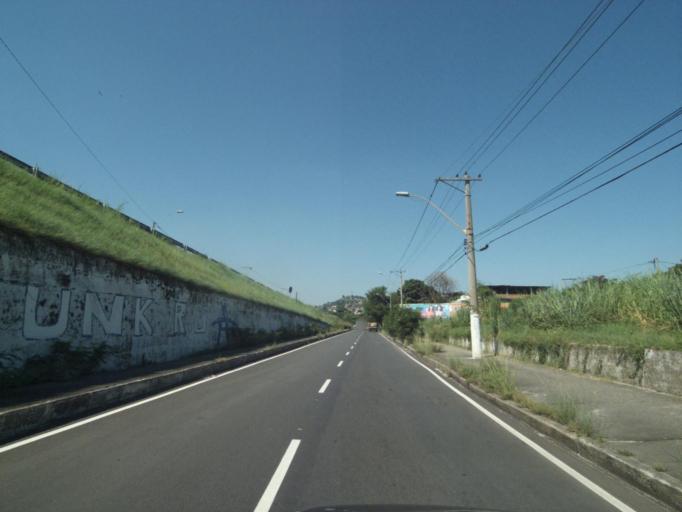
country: BR
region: Rio de Janeiro
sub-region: Niteroi
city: Niteroi
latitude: -22.8600
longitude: -43.1056
